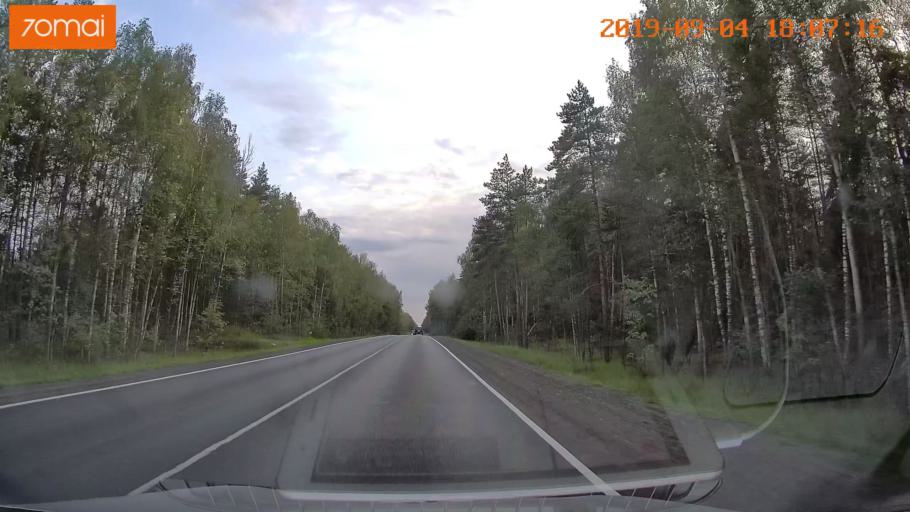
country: RU
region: Moskovskaya
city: Khorlovo
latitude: 55.4211
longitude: 38.8032
